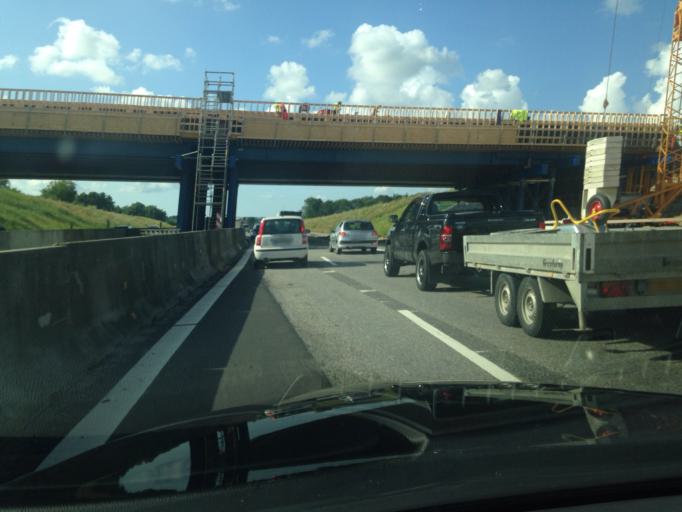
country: DK
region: Capital Region
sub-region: Rudersdal Kommune
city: Trorod
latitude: 55.8324
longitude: 12.5231
